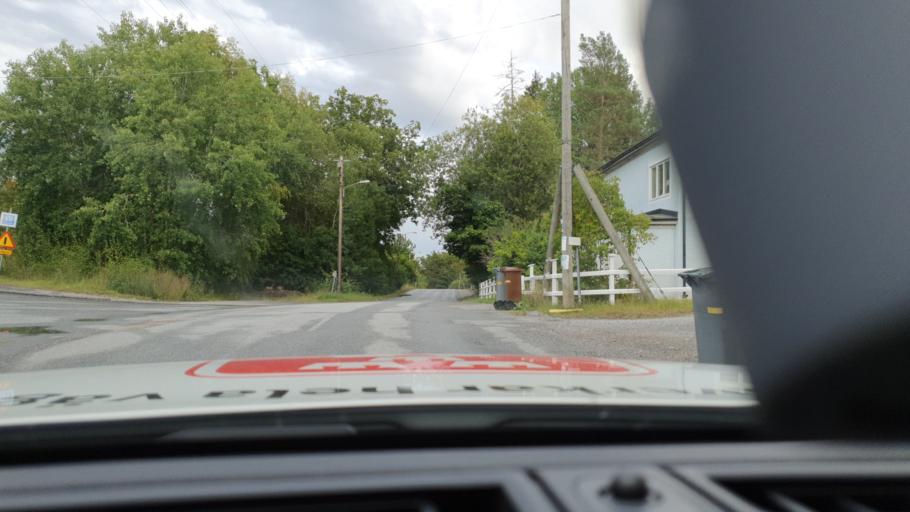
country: SE
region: Stockholm
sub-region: Vaxholms Kommun
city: Vaxholm
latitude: 59.3926
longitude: 18.4144
